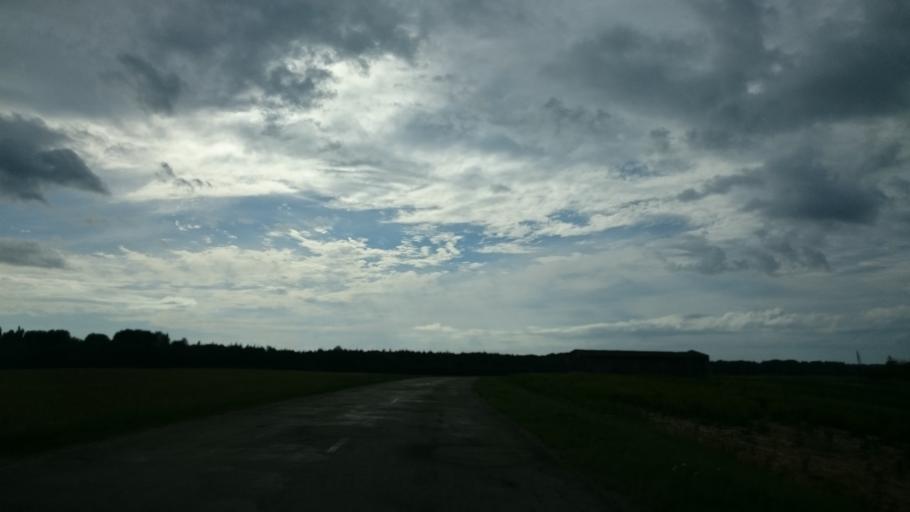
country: LV
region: Seja
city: Loja
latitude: 57.2346
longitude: 24.5493
